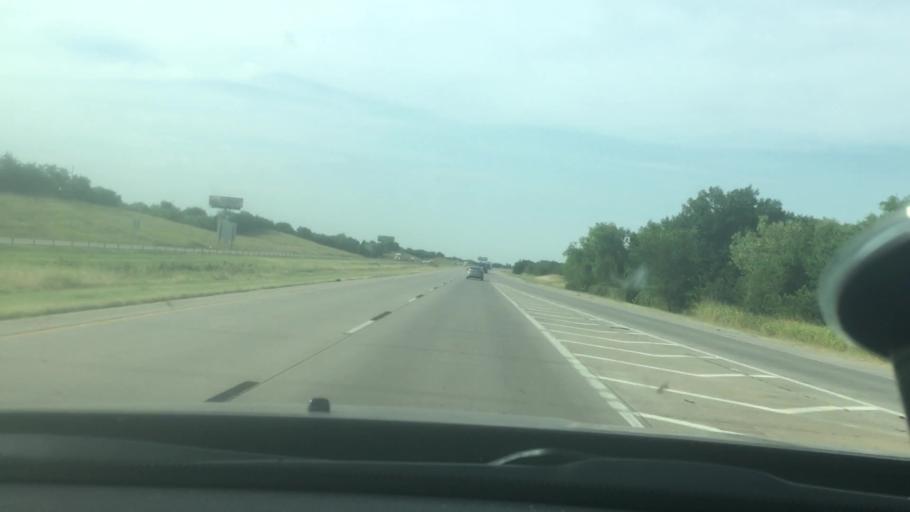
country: US
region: Oklahoma
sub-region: Carter County
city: Ardmore
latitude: 34.3008
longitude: -97.1599
